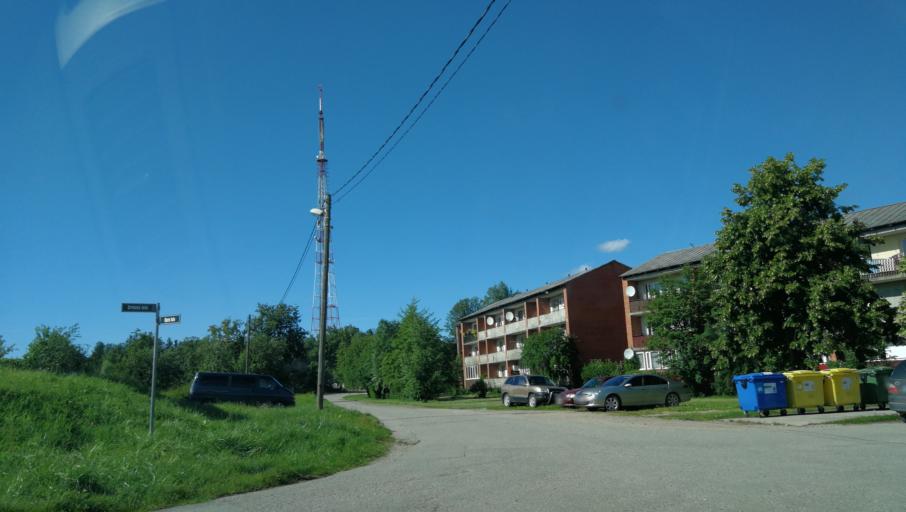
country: LV
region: Cesvaine
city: Cesvaine
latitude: 56.9660
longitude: 26.3021
